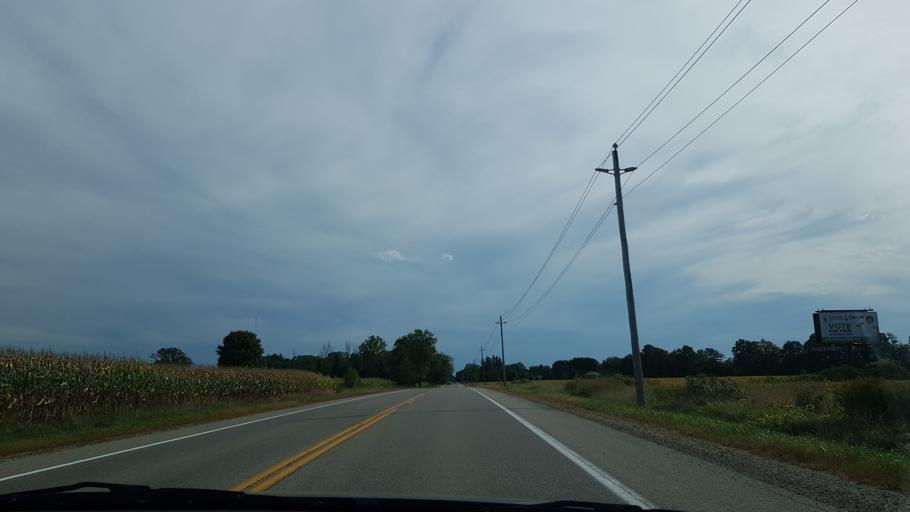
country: CA
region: Ontario
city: Delaware
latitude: 42.9896
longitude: -81.3906
